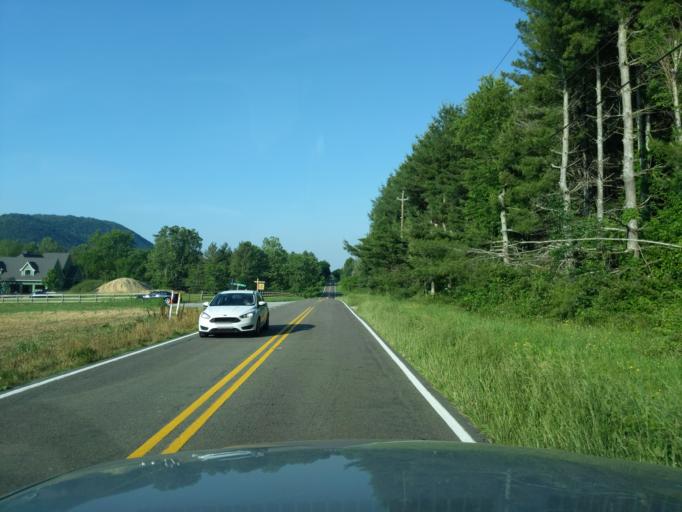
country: US
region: North Carolina
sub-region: Henderson County
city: Hoopers Creek
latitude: 35.4751
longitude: -82.4518
